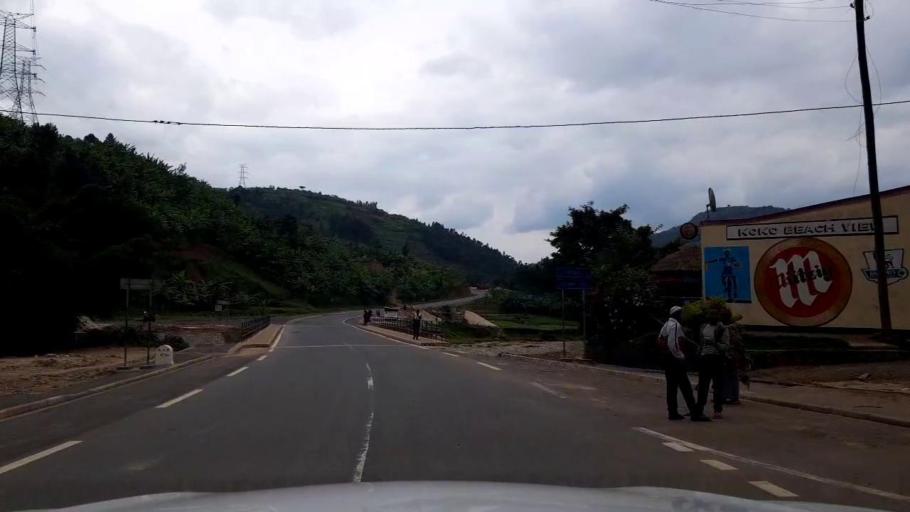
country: RW
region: Western Province
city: Kibuye
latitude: -1.9154
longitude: 29.3689
